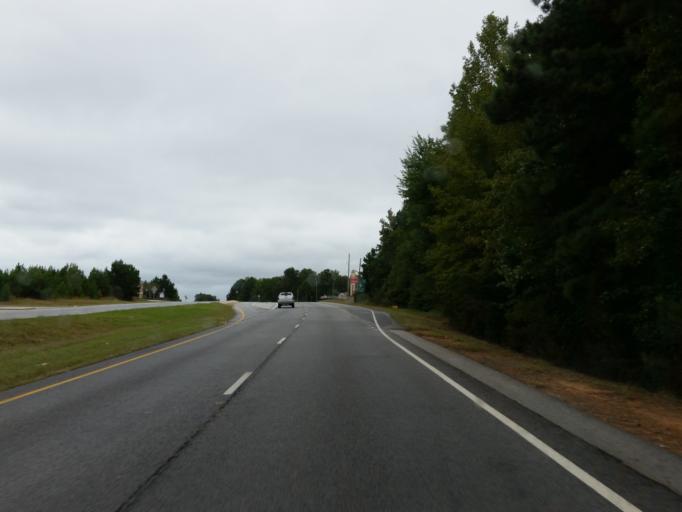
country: US
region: Georgia
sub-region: Henry County
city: Hampton
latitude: 33.3973
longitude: -84.3119
